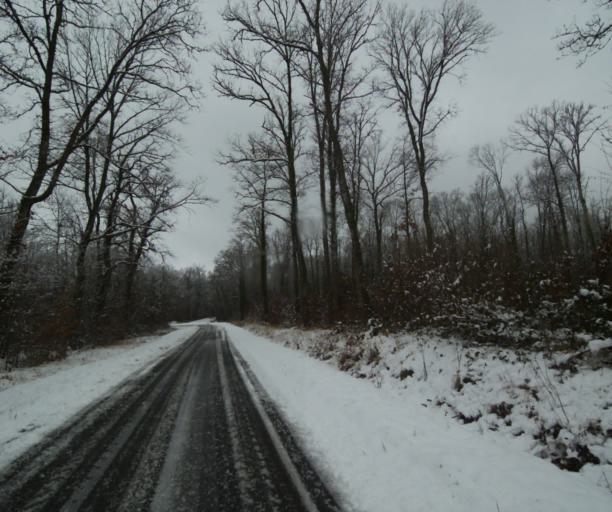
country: FR
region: Champagne-Ardenne
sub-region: Departement de la Haute-Marne
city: Wassy
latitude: 48.4576
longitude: 4.9382
